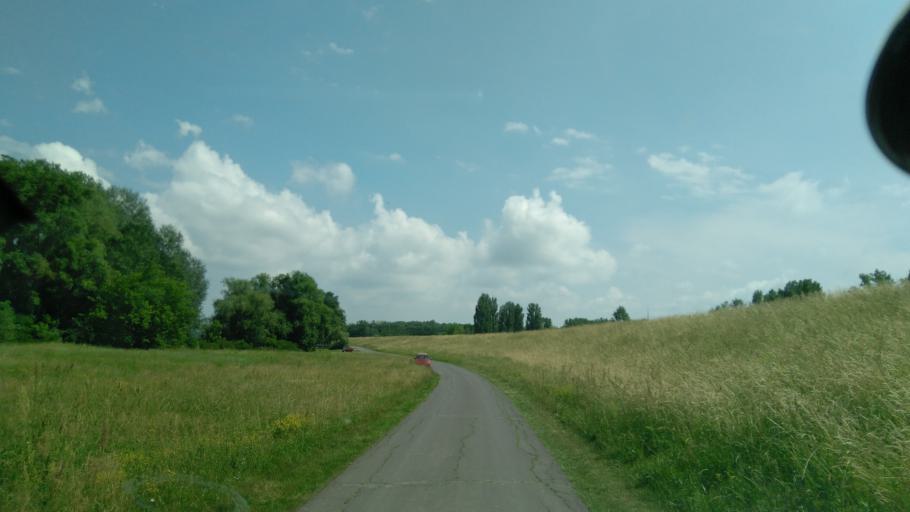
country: HU
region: Bekes
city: Bekes
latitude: 46.7622
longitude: 21.1516
